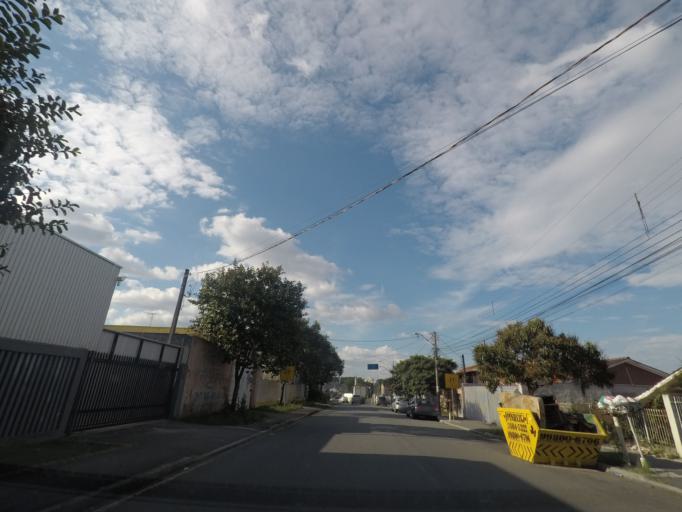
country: BR
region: Parana
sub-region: Sao Jose Dos Pinhais
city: Sao Jose dos Pinhais
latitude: -25.5027
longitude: -49.2767
